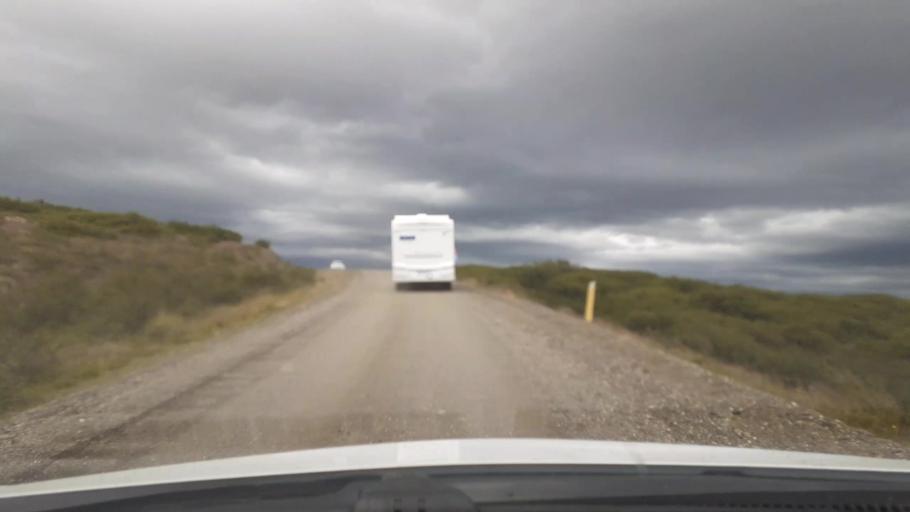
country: IS
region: West
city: Borgarnes
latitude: 64.5574
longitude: -21.6242
